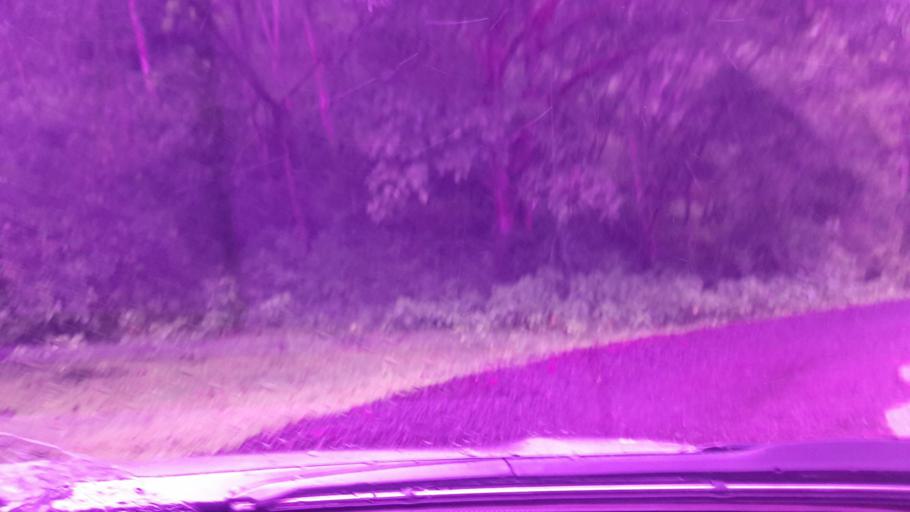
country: ET
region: Oromiya
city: Metu
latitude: 8.4757
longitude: 35.6405
